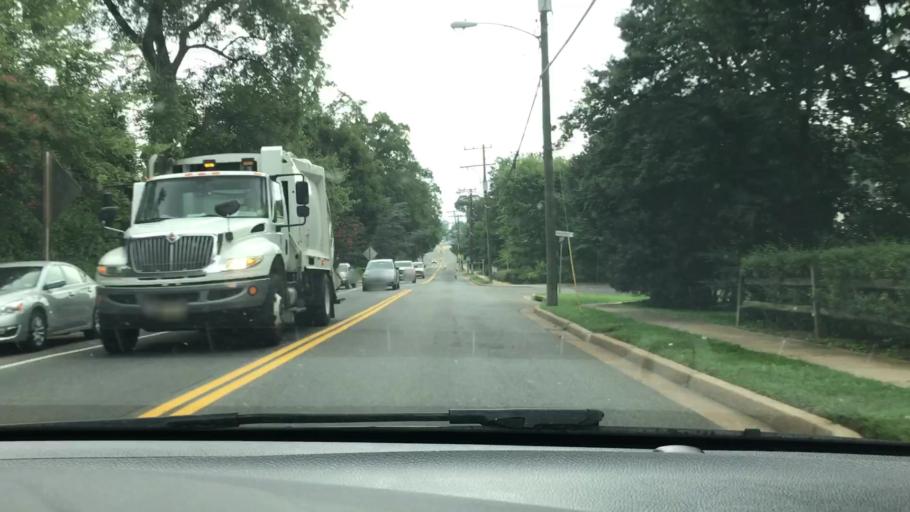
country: US
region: Virginia
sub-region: Arlington County
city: Arlington
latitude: 38.8852
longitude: -77.1240
